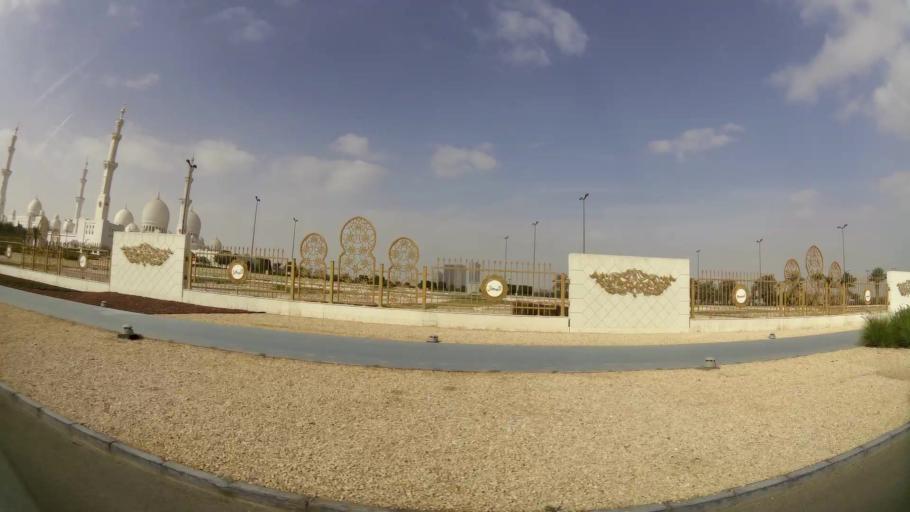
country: AE
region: Abu Dhabi
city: Abu Dhabi
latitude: 24.4157
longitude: 54.4779
